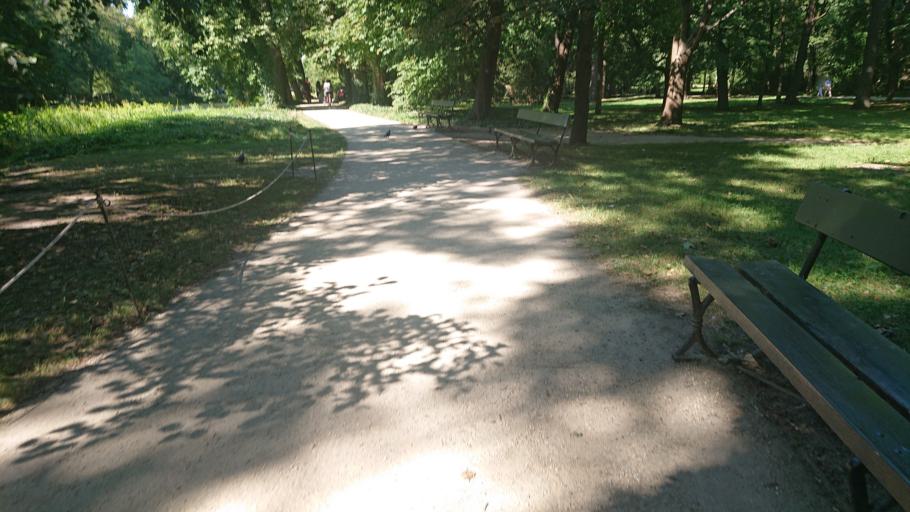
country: PL
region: Masovian Voivodeship
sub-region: Warszawa
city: Mokotow
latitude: 52.2114
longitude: 21.0365
